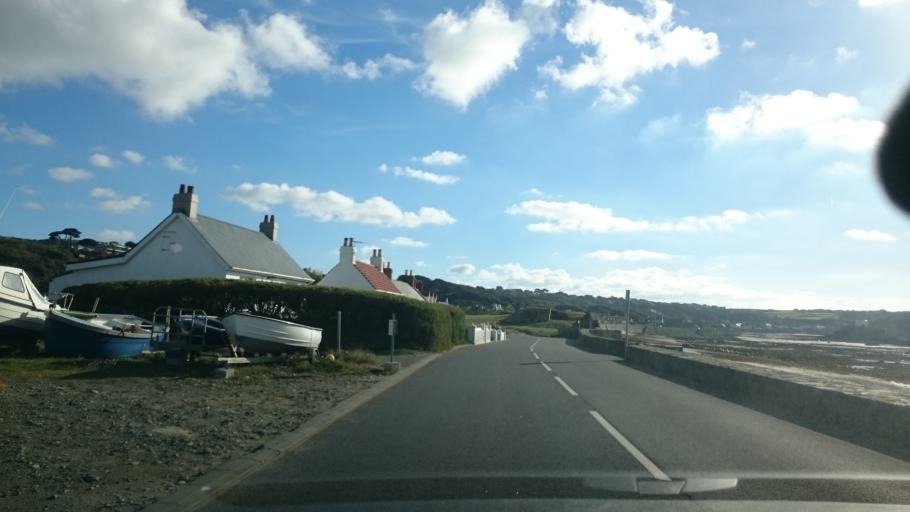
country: GG
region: St Peter Port
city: Saint Peter Port
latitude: 49.4457
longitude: -2.6492
